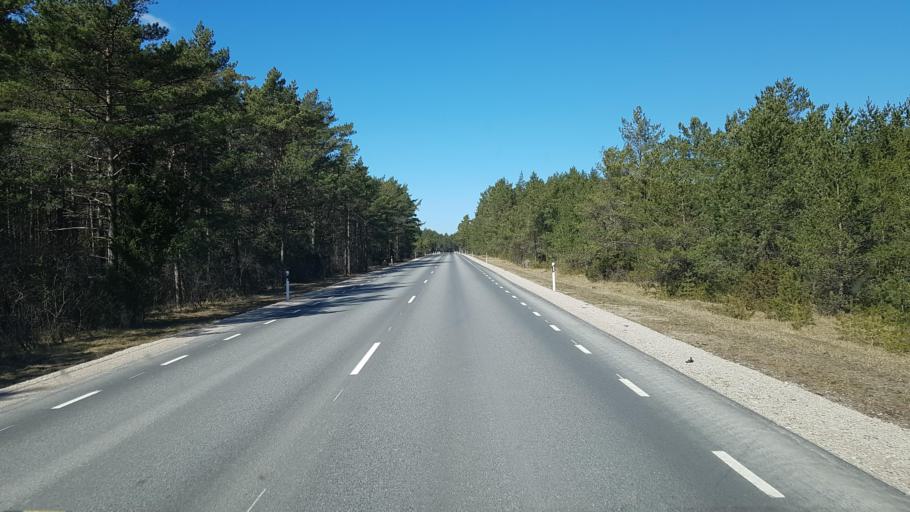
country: EE
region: Saare
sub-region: Kuressaare linn
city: Kuressaare
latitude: 58.2966
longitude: 22.2665
